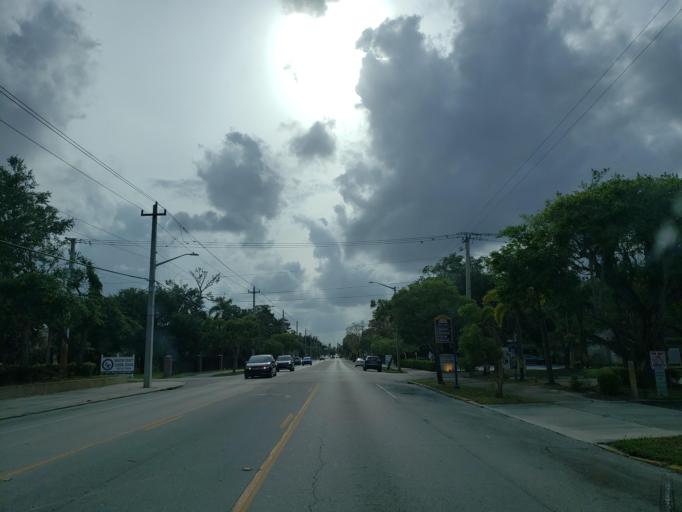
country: US
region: Florida
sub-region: Martin County
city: Stuart
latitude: 27.1975
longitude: -80.2446
